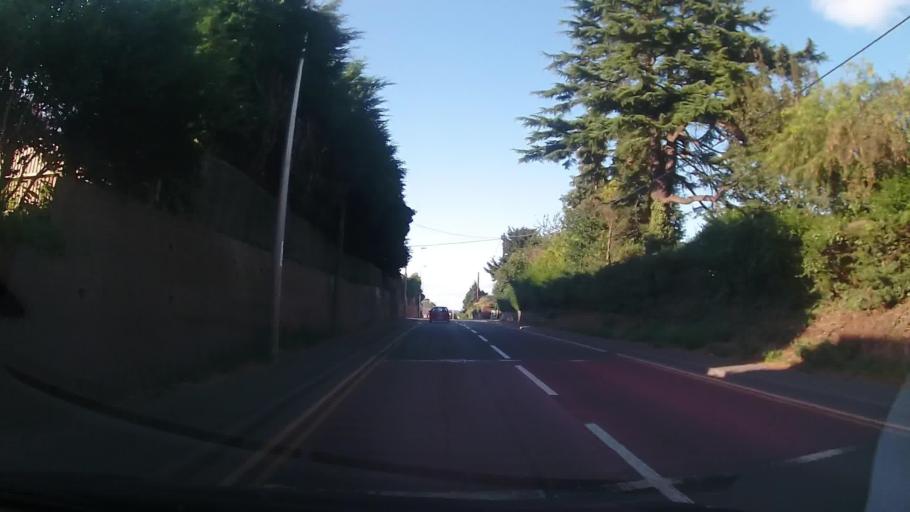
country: GB
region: England
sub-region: Shropshire
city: Bayston Hill
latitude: 52.6734
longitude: -2.7608
